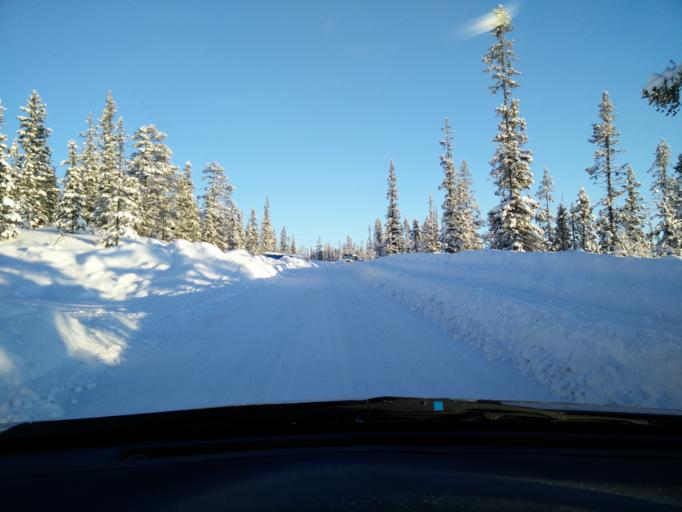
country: SE
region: Jaemtland
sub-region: Bergs Kommun
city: Hoverberg
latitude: 62.4971
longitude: 14.1193
